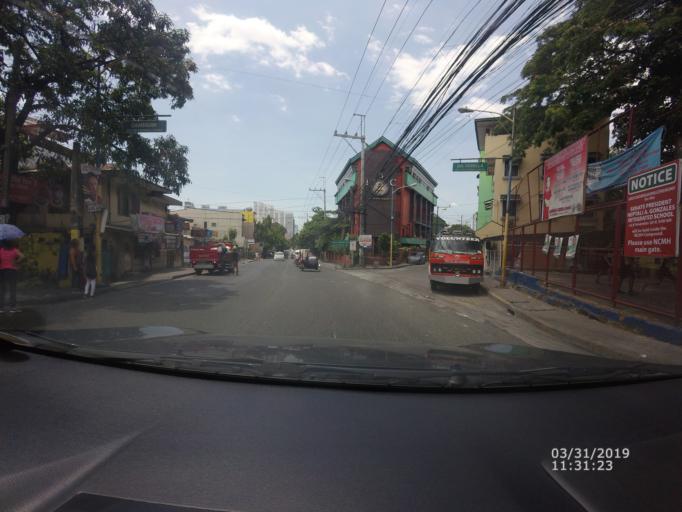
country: PH
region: Metro Manila
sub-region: Mandaluyong
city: Mandaluyong City
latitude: 14.5782
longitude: 121.0428
